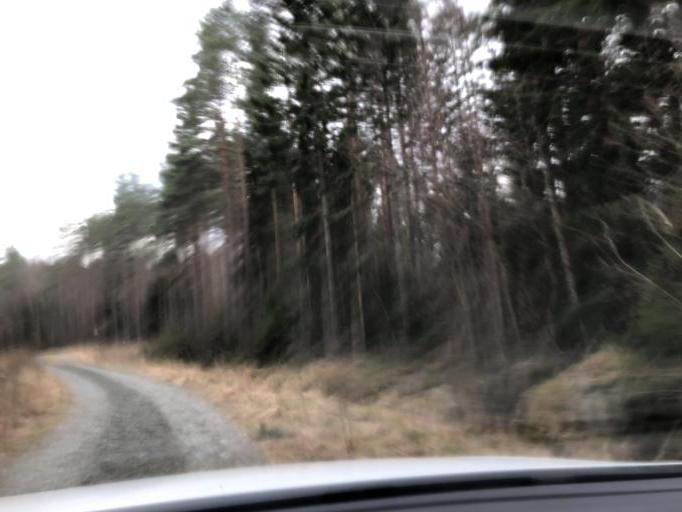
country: SE
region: Uppsala
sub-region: Heby Kommun
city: OEstervala
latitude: 60.3340
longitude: 17.1714
